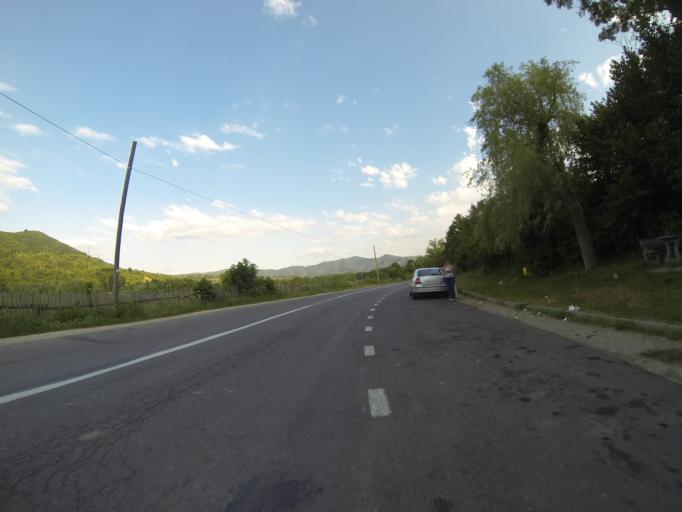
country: RO
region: Brasov
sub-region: Comuna Sinca Noua
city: Sinca Noua
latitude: 45.7329
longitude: 25.2321
